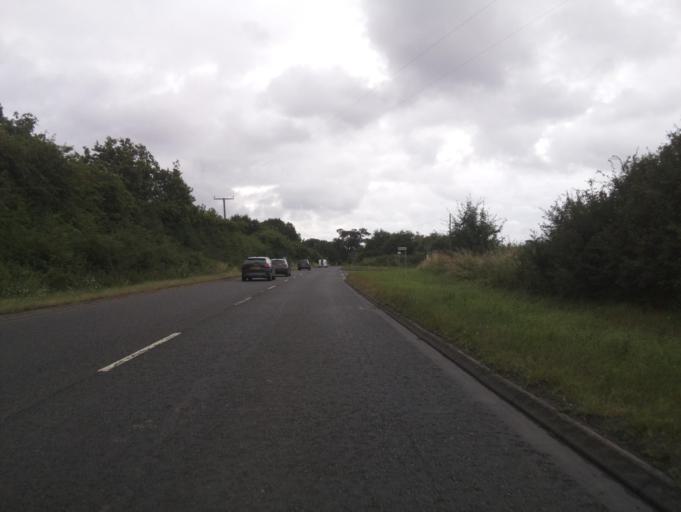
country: GB
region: England
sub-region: Worcestershire
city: Fernhill Heath
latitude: 52.2244
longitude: -2.1654
